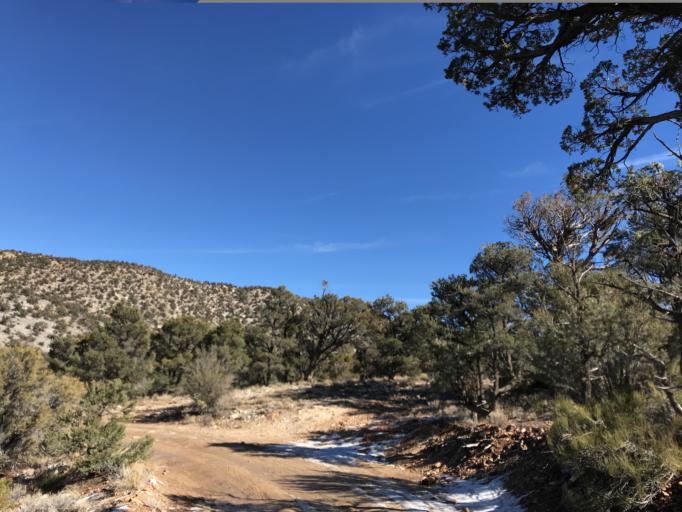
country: US
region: California
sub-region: San Bernardino County
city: Big Bear City
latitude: 34.2547
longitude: -116.7178
